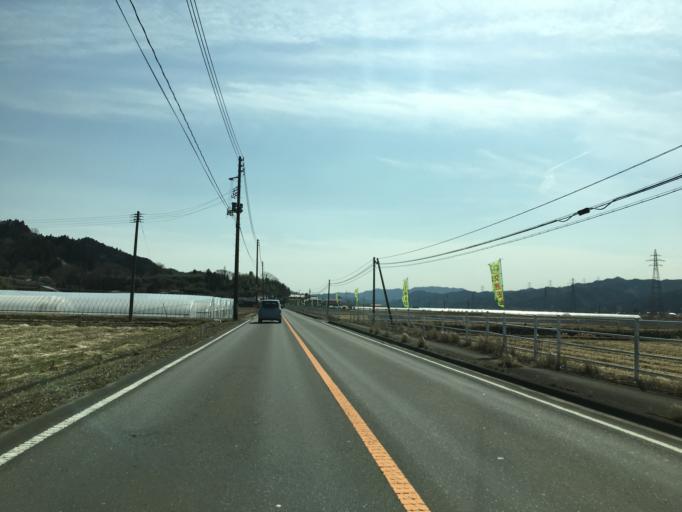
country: JP
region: Ibaraki
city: Daigo
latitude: 36.9208
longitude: 140.4159
